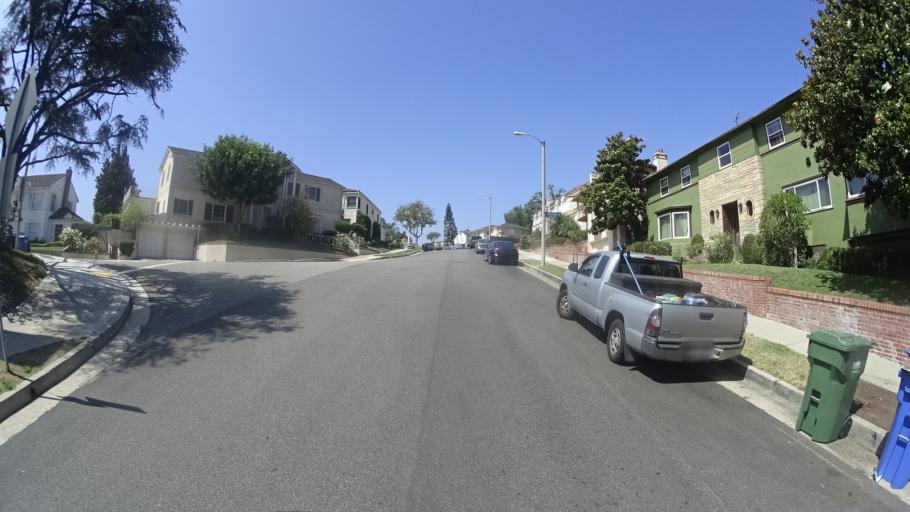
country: US
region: California
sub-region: Los Angeles County
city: View Park-Windsor Hills
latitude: 34.0047
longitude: -118.3393
